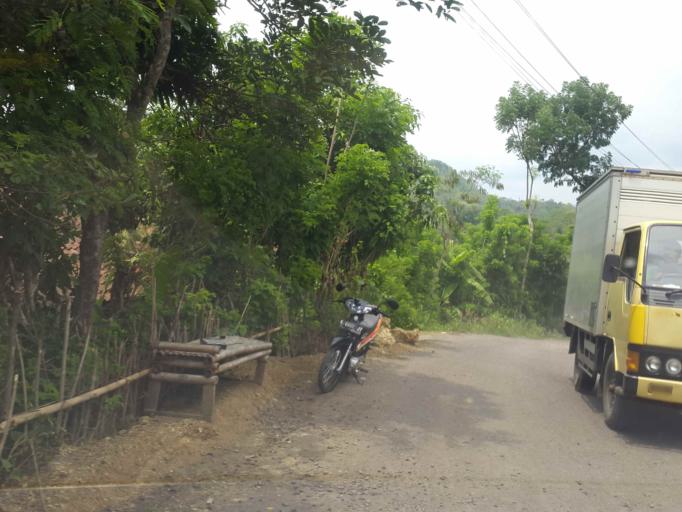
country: ID
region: Central Java
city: Pasanggrahan
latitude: -7.3792
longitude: 108.8922
